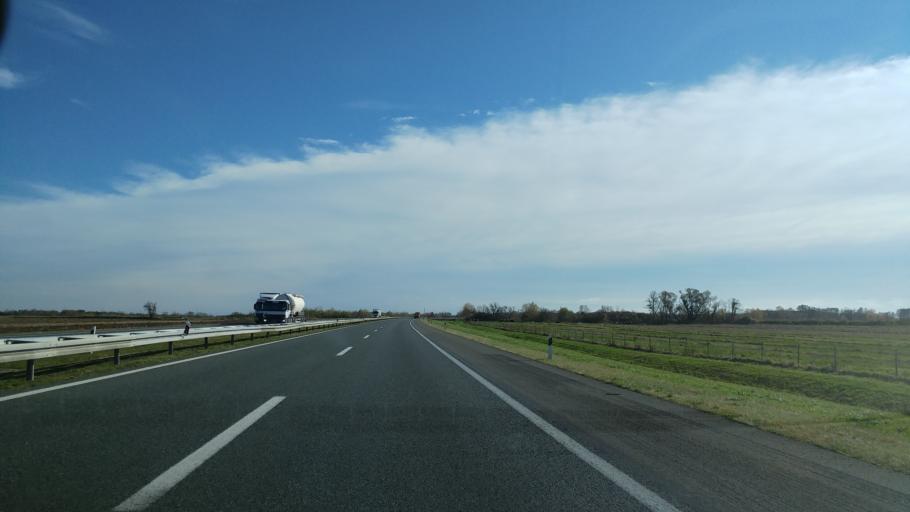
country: HR
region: Brodsko-Posavska
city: Okucani
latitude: 45.2579
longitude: 17.1688
